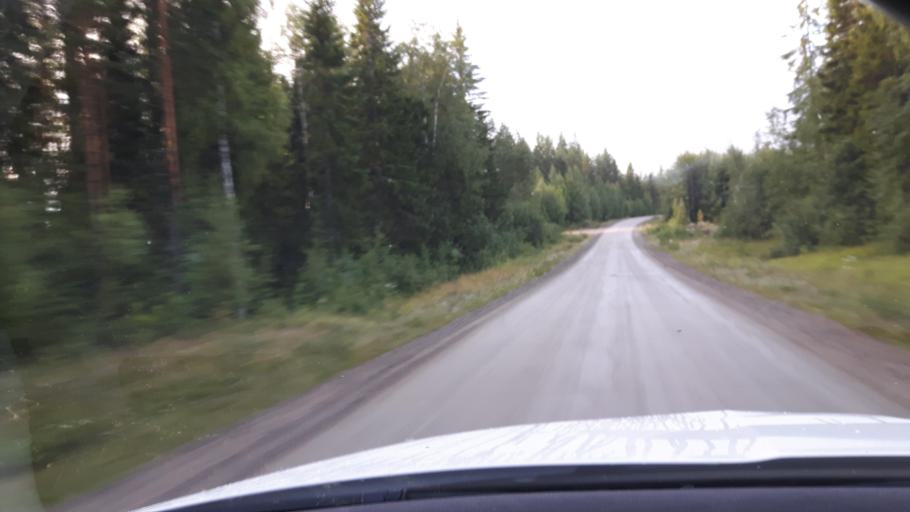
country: SE
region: Gaevleborg
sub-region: Ljusdals Kommun
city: Farila
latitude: 62.0163
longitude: 15.8380
